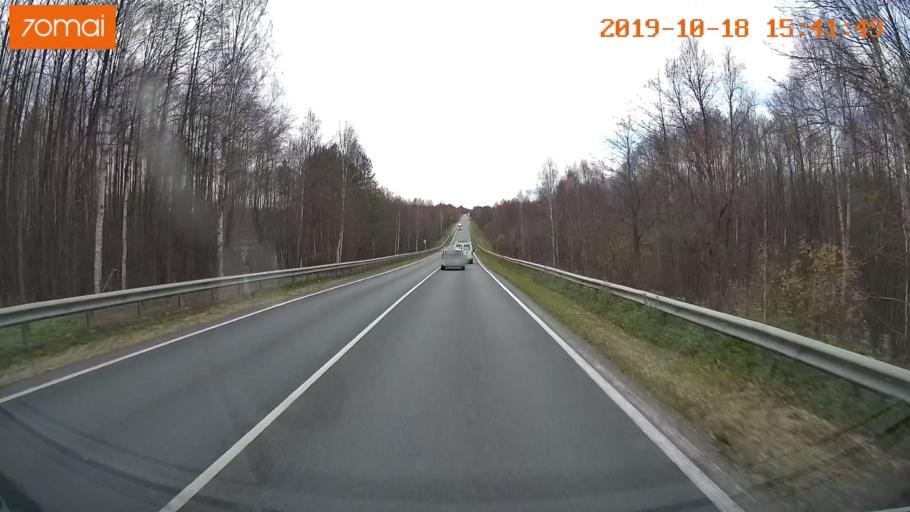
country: RU
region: Vladimir
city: Golovino
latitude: 55.9495
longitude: 40.5772
